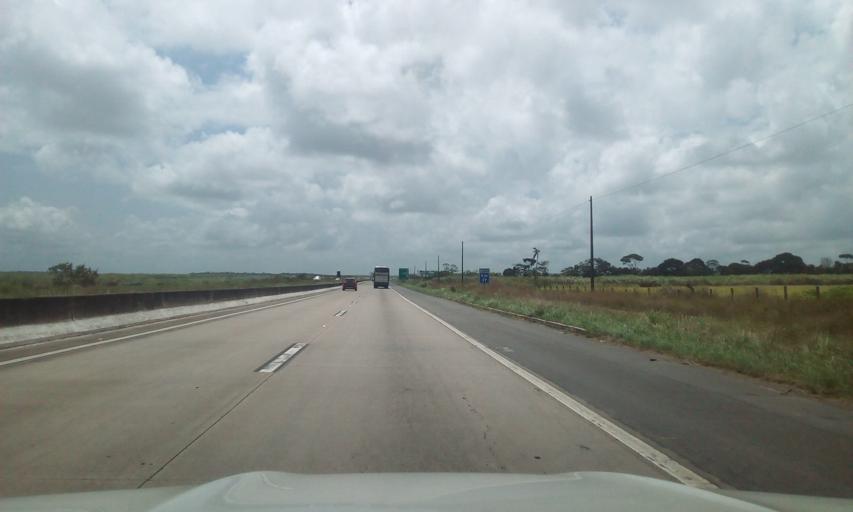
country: BR
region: Pernambuco
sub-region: Goiana
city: Goiana
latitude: -7.6399
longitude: -34.9564
